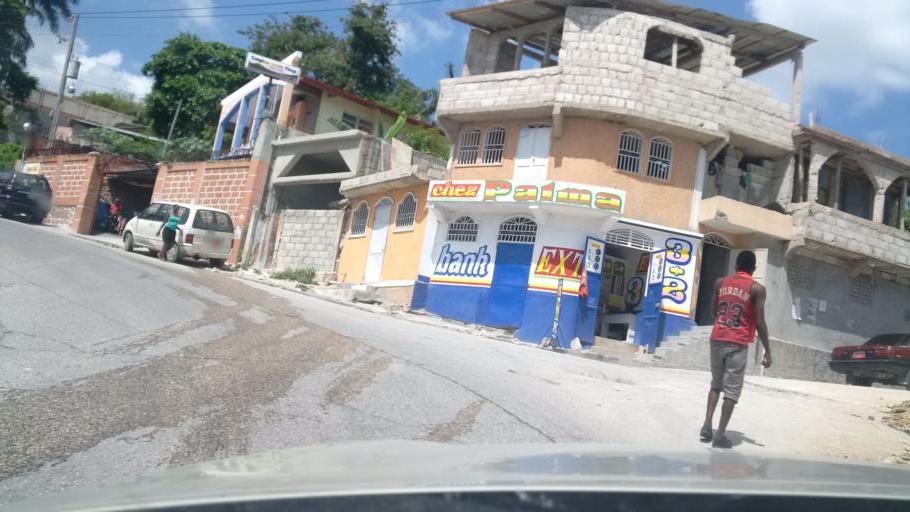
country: HT
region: Ouest
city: Delmas 73
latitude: 18.5414
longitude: -72.3182
